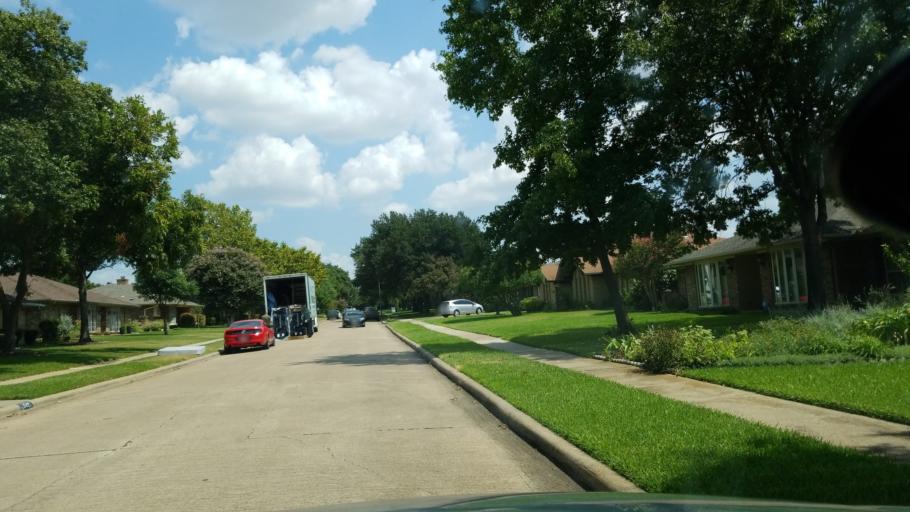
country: US
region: Texas
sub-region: Dallas County
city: Richardson
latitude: 32.9268
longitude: -96.7278
